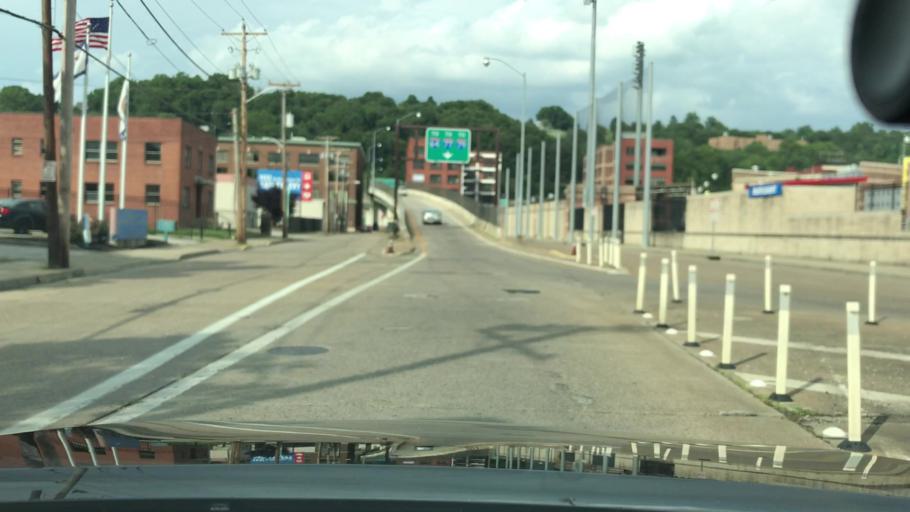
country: US
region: West Virginia
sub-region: Kanawha County
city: Charleston
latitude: 38.3490
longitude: -81.6266
